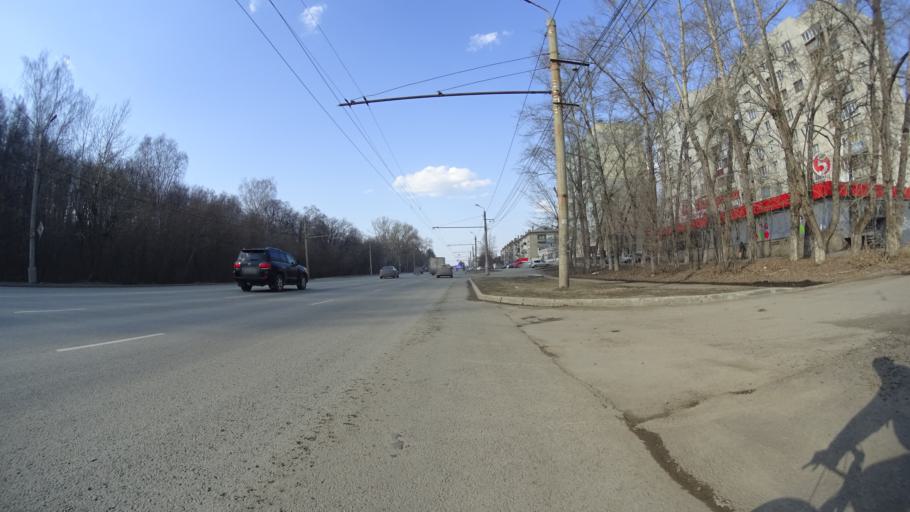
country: RU
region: Chelyabinsk
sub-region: Gorod Chelyabinsk
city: Chelyabinsk
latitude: 55.1223
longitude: 61.3636
